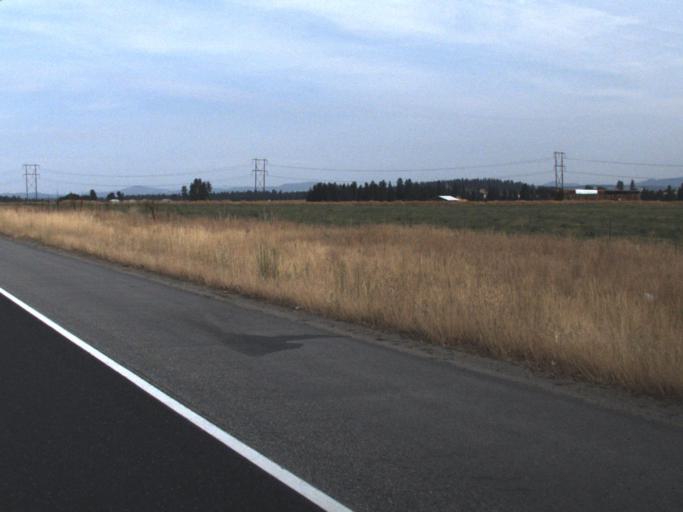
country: US
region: Washington
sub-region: Spokane County
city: Fairwood
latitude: 47.8438
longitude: -117.4218
